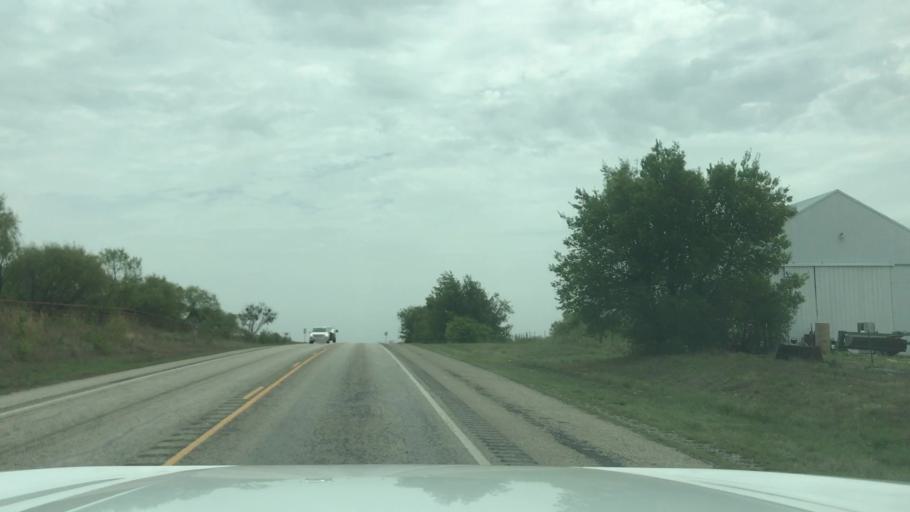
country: US
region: Texas
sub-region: Erath County
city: Dublin
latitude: 32.0583
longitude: -98.2028
